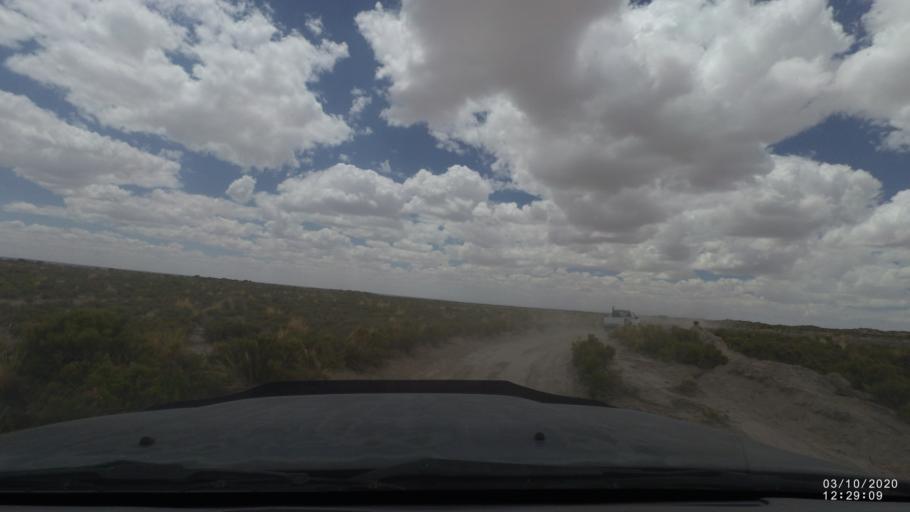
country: BO
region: Oruro
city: Poopo
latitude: -18.6895
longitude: -67.5490
